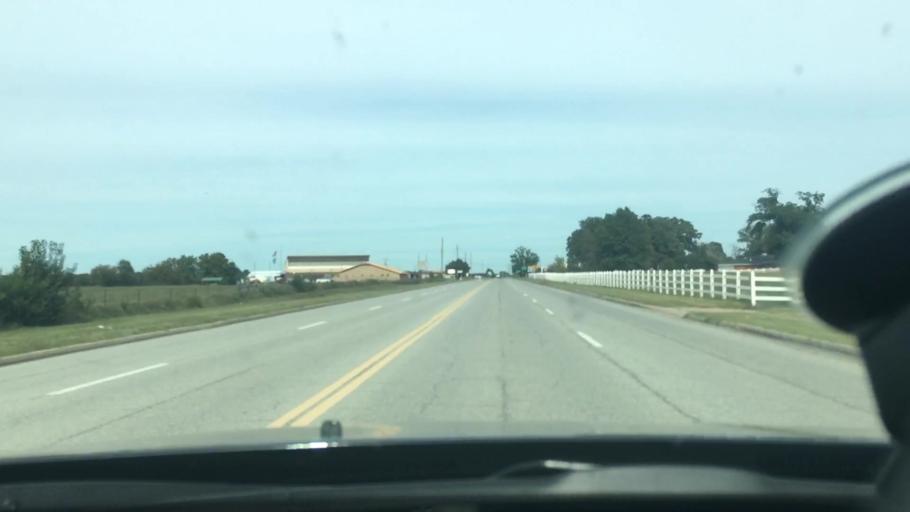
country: US
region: Oklahoma
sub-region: Atoka County
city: Atoka
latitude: 34.3899
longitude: -96.1455
